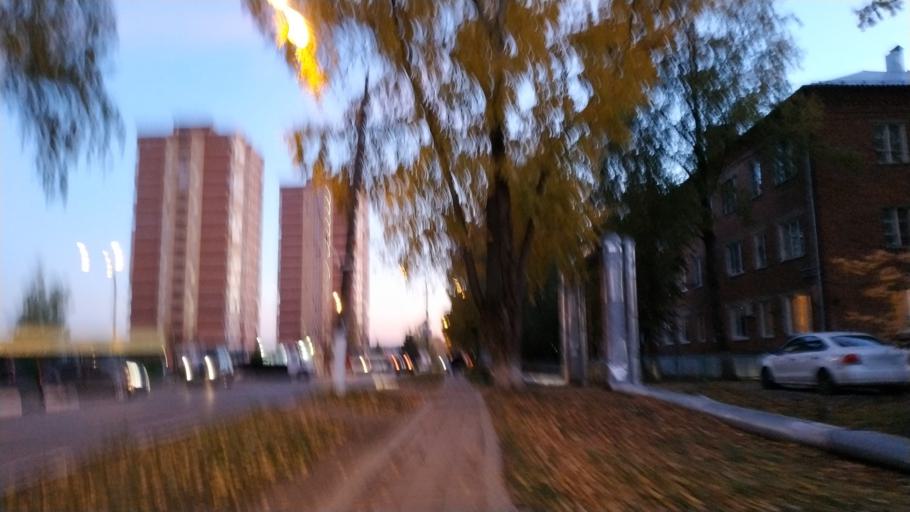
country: RU
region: Moskovskaya
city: Lobnya
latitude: 56.0200
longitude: 37.4220
